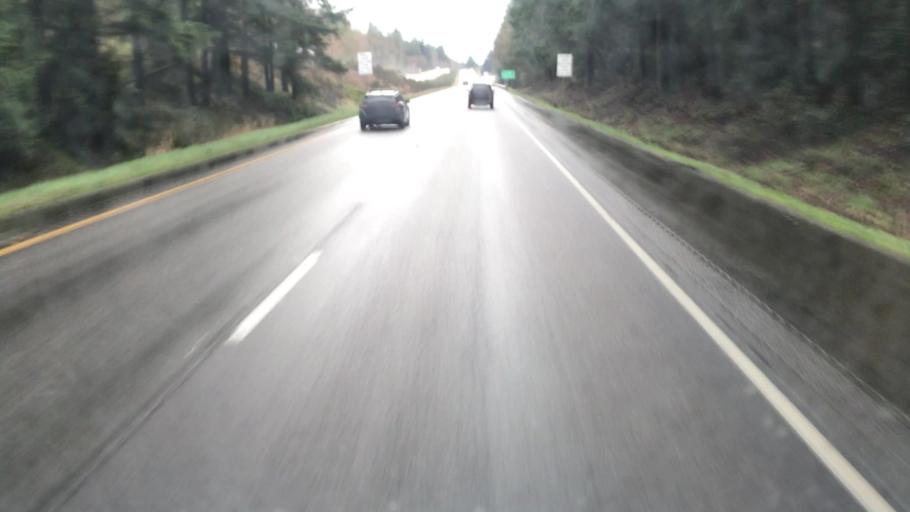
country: US
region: Washington
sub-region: Kitsap County
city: Burley
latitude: 47.4397
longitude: -122.6229
